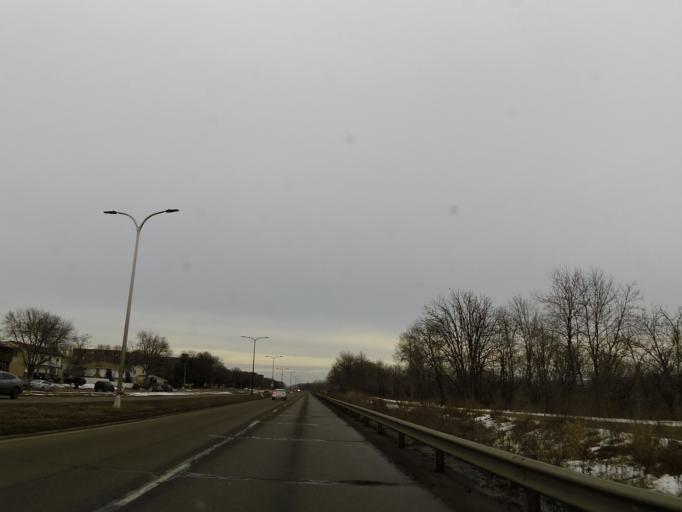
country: US
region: Minnesota
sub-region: Dakota County
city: Mendota Heights
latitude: 44.8992
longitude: -93.1657
